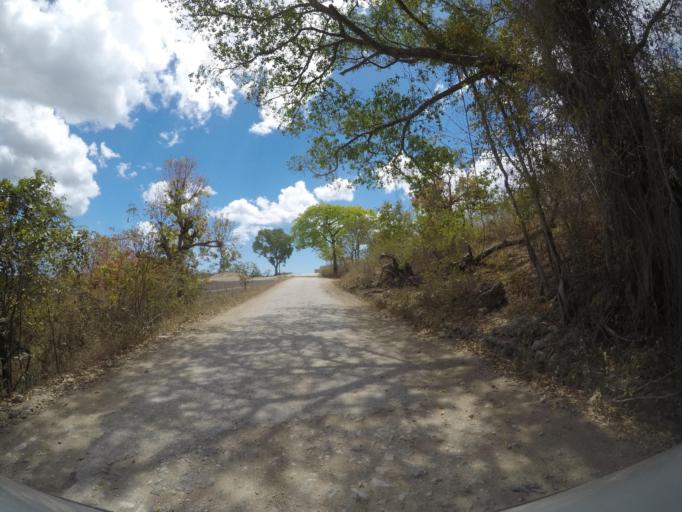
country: TL
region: Baucau
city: Baucau
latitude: -8.4852
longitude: 126.6207
